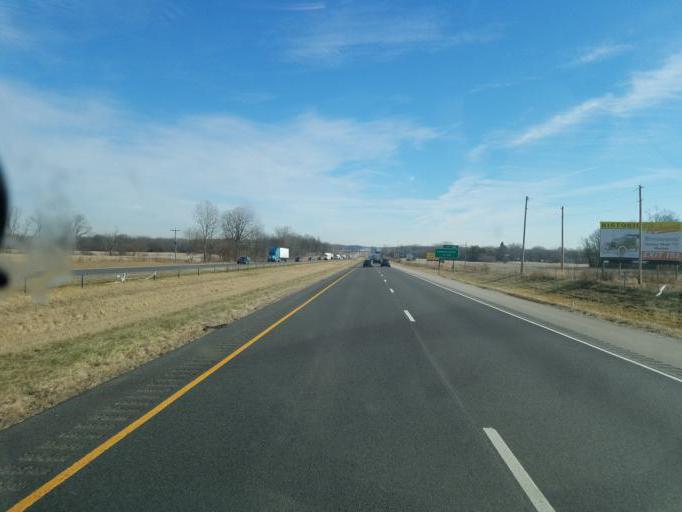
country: US
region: Indiana
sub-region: Wayne County
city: Centerville
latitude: 39.8593
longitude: -85.0117
